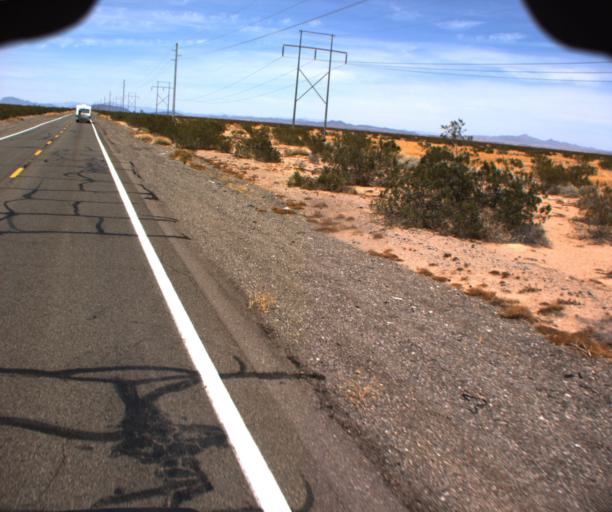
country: US
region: Arizona
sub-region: La Paz County
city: Parker
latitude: 33.9304
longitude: -114.2169
